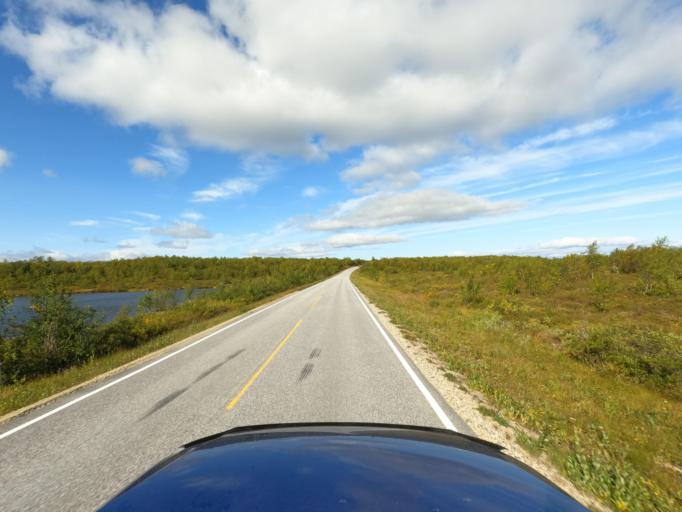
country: NO
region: Finnmark Fylke
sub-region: Karasjok
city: Karasjohka
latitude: 69.6130
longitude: 25.3047
